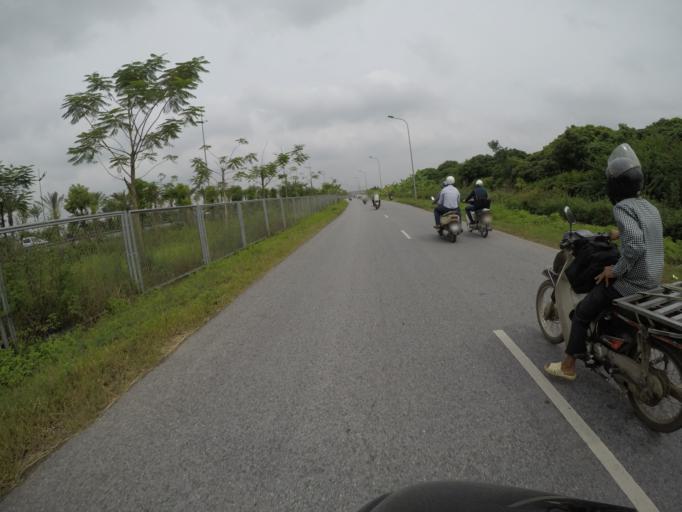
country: VN
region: Ha Noi
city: Dong Anh
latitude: 21.1587
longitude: 105.8198
